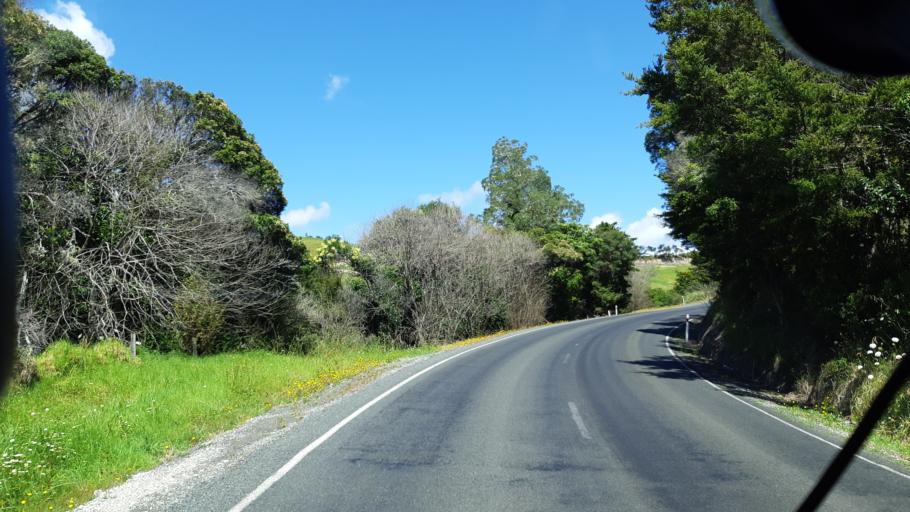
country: NZ
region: Northland
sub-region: Far North District
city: Kaitaia
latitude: -35.2712
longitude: 173.4845
